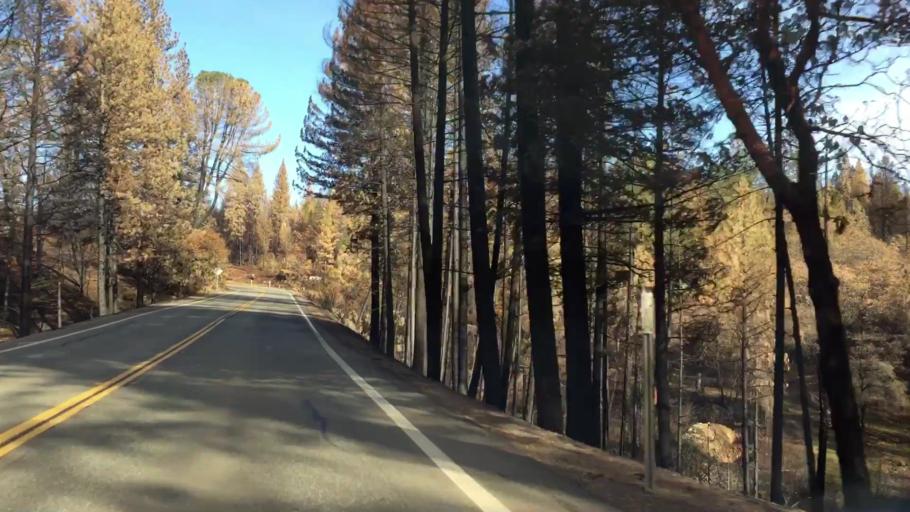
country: US
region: California
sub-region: Butte County
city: Magalia
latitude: 39.7303
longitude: -121.4942
